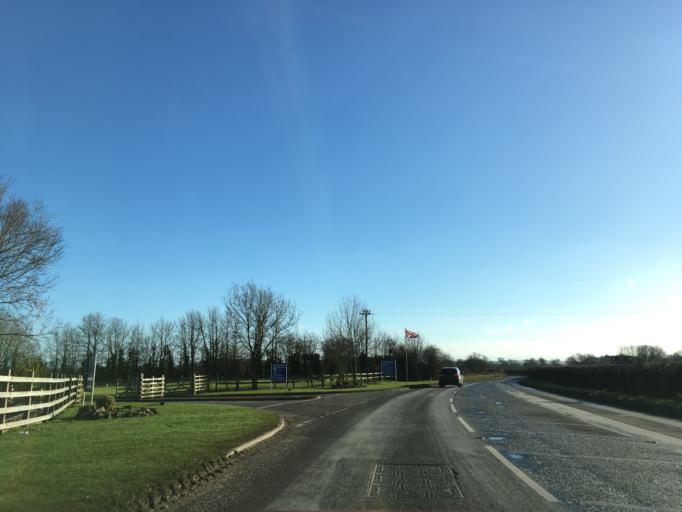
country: GB
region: England
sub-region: Wiltshire
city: Biddestone
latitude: 51.4797
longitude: -2.1831
